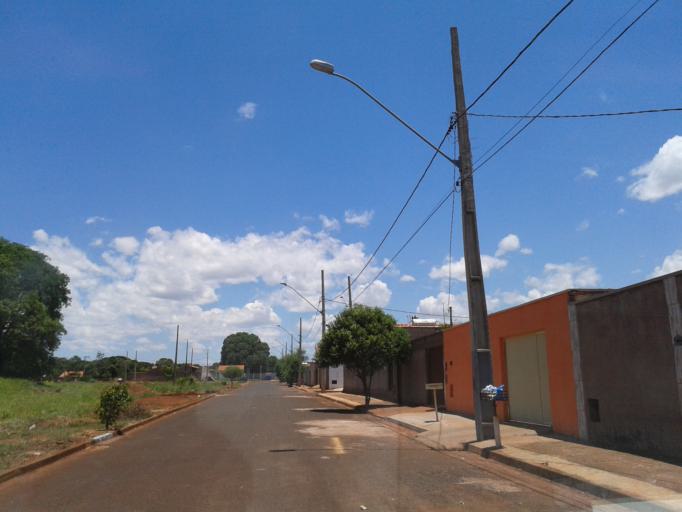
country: BR
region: Minas Gerais
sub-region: Centralina
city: Centralina
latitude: -18.7153
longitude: -49.2046
